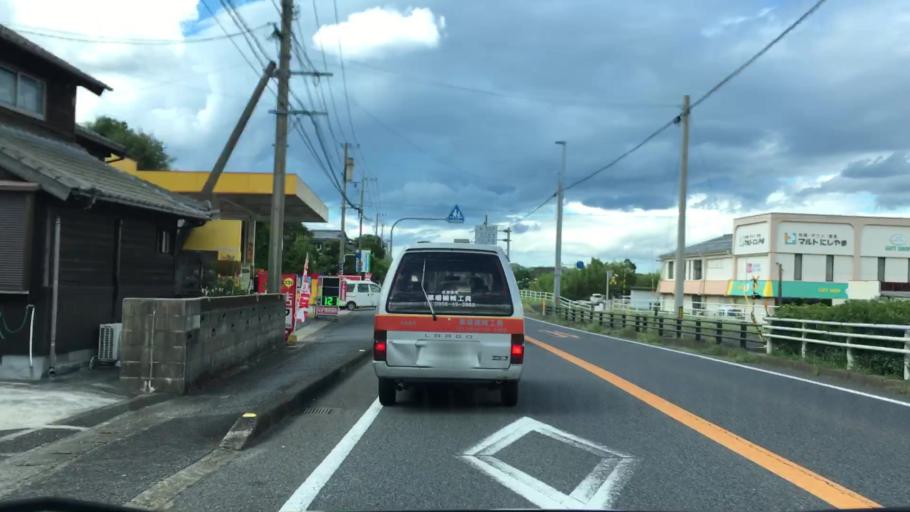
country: JP
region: Saga Prefecture
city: Imaricho-ko
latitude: 33.2066
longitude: 129.8505
